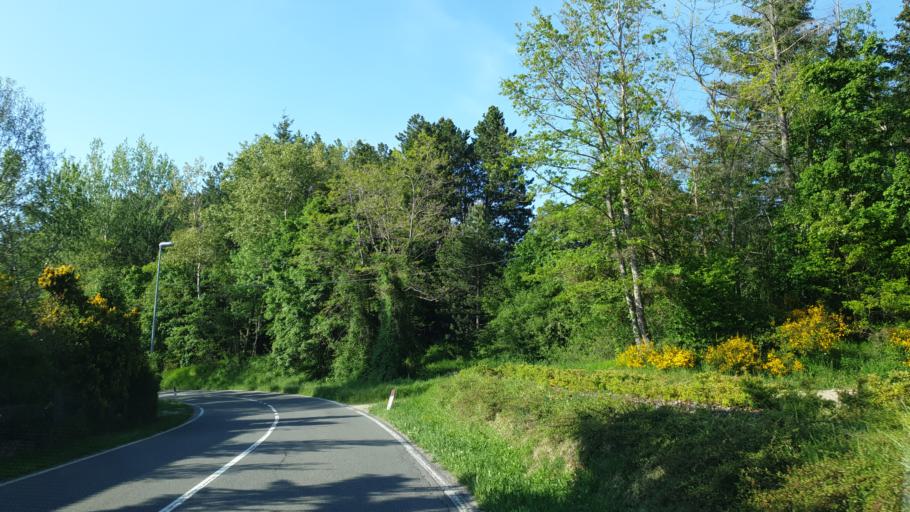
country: IT
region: Tuscany
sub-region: Province of Arezzo
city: Montemignaio
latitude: 43.7851
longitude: 11.6505
